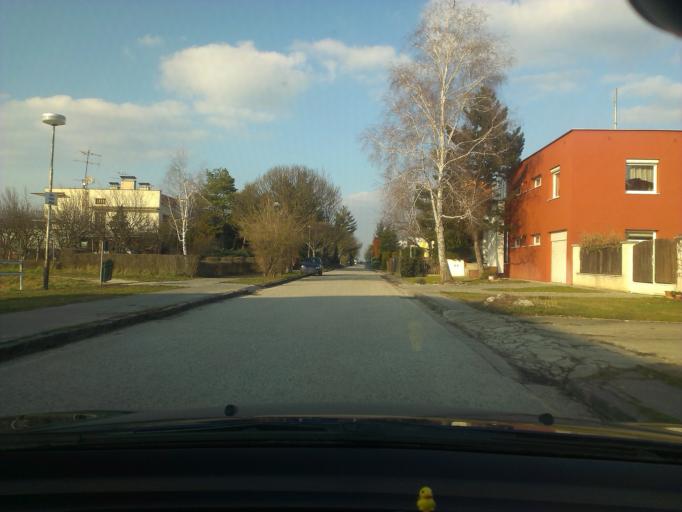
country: SK
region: Trnavsky
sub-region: Okres Trnava
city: Piestany
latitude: 48.6035
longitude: 17.8220
